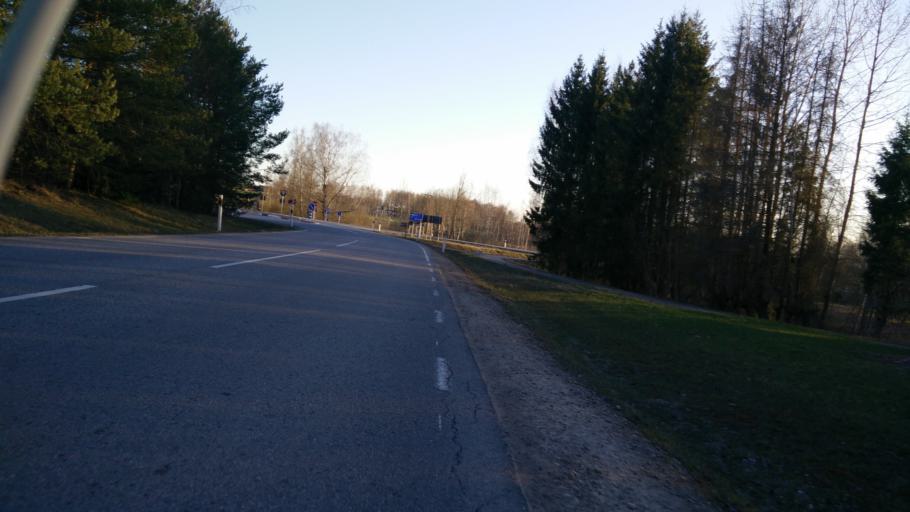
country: EE
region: Polvamaa
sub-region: Polva linn
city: Polva
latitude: 58.0610
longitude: 26.8977
